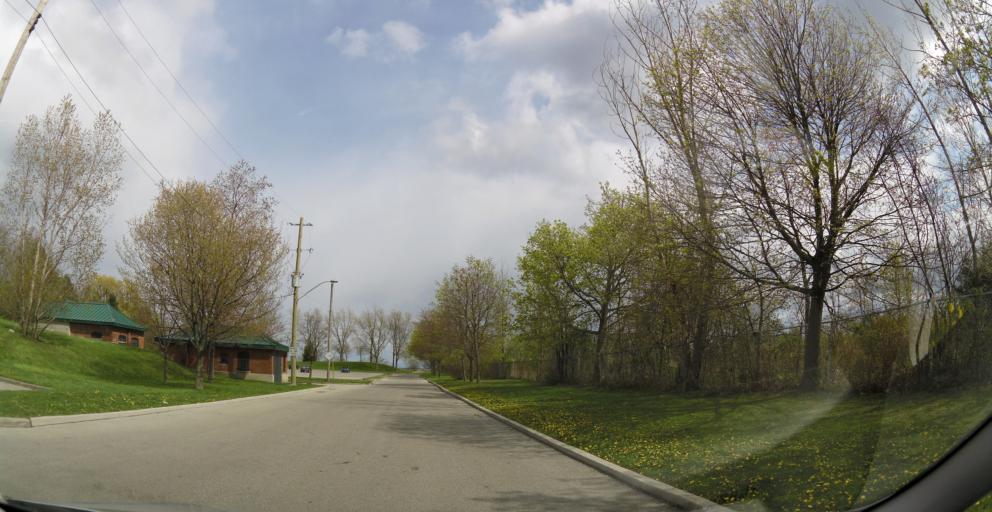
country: CA
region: Ontario
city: Mississauga
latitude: 43.5458
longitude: -79.5857
